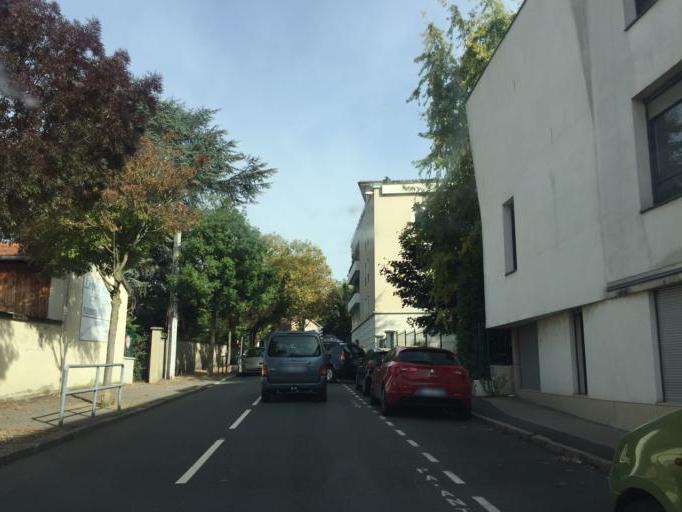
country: FR
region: Rhone-Alpes
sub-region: Departement du Rhone
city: Neuville-sur-Saone
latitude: 45.8770
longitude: 4.8418
